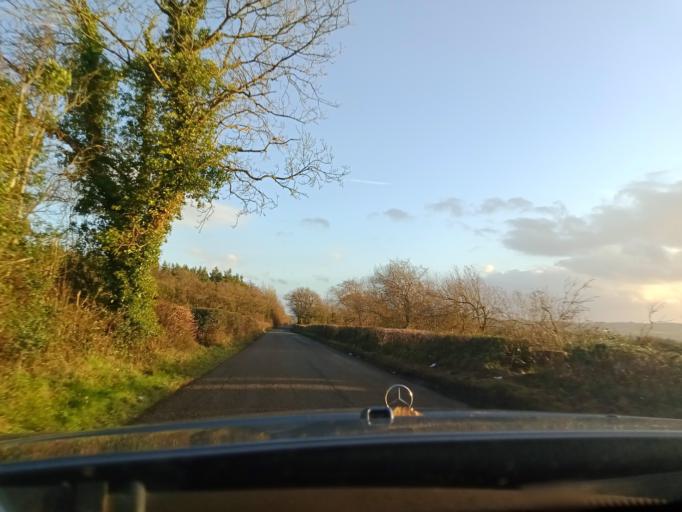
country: IE
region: Leinster
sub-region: Kilkenny
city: Callan
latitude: 52.4949
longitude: -7.3318
